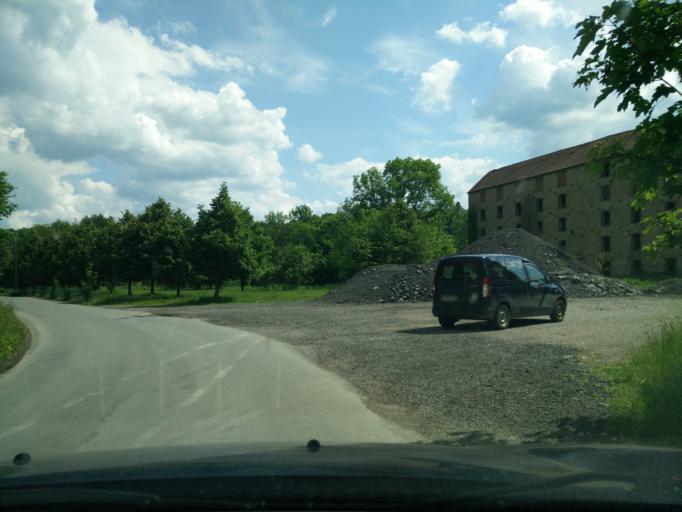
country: BE
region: Wallonia
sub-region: Province de Namur
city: Couvin
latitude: 50.0855
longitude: 4.5647
